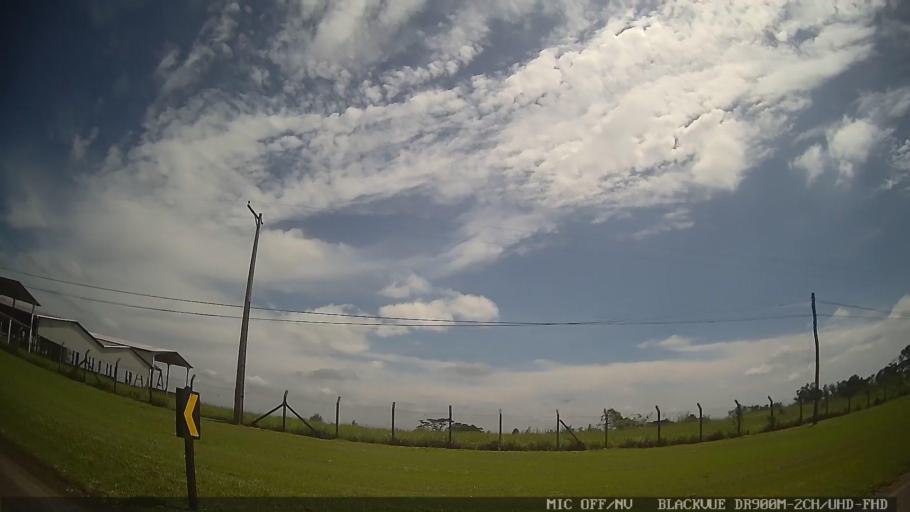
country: BR
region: Sao Paulo
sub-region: Laranjal Paulista
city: Laranjal Paulista
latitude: -23.0780
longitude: -47.7982
